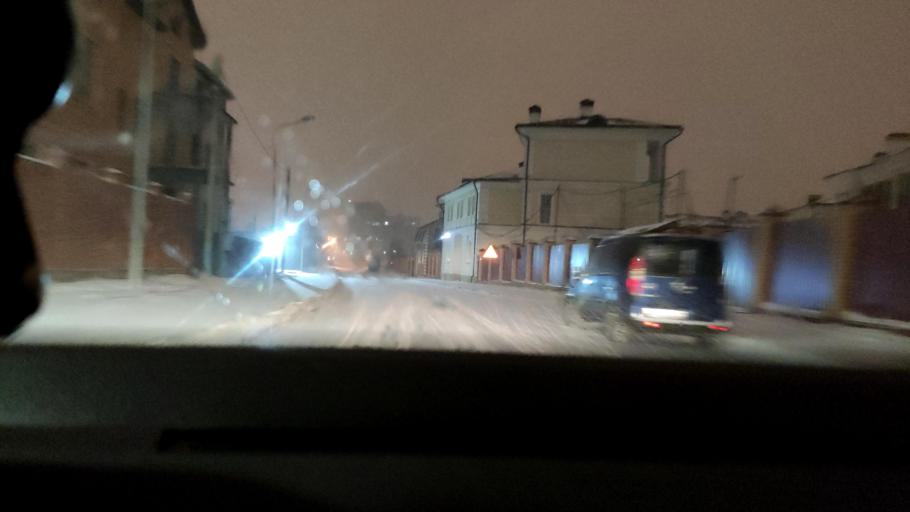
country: RU
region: Moskovskaya
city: Mosrentgen
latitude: 55.6285
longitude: 37.4562
